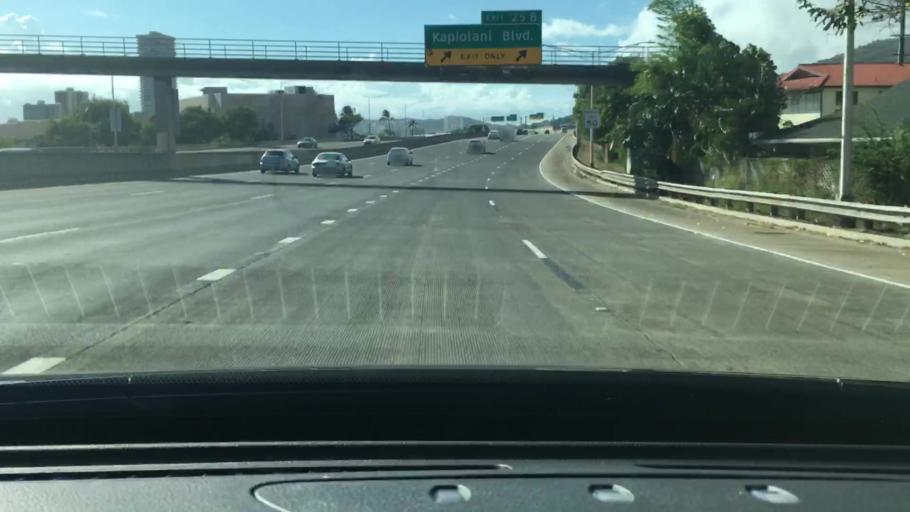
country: US
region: Hawaii
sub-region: Honolulu County
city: Honolulu
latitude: 21.2862
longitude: -157.8112
